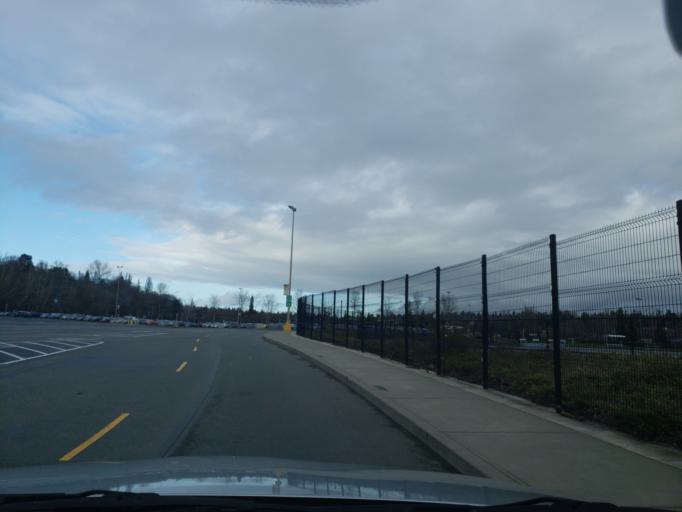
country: US
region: Washington
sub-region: King County
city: Seattle
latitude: 47.6564
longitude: -122.2994
